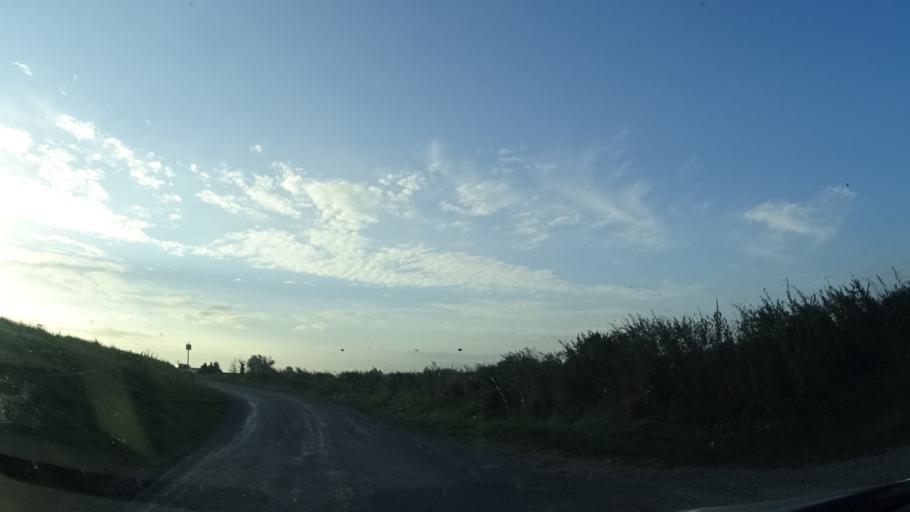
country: BE
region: Wallonia
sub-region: Province du Hainaut
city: Beaumont
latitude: 50.2389
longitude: 4.2702
